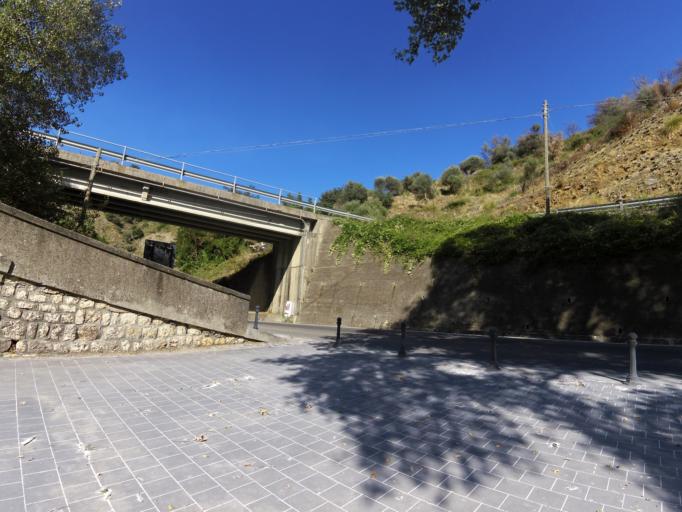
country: IT
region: Calabria
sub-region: Provincia di Reggio Calabria
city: Bivongi
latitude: 38.4864
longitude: 16.4613
